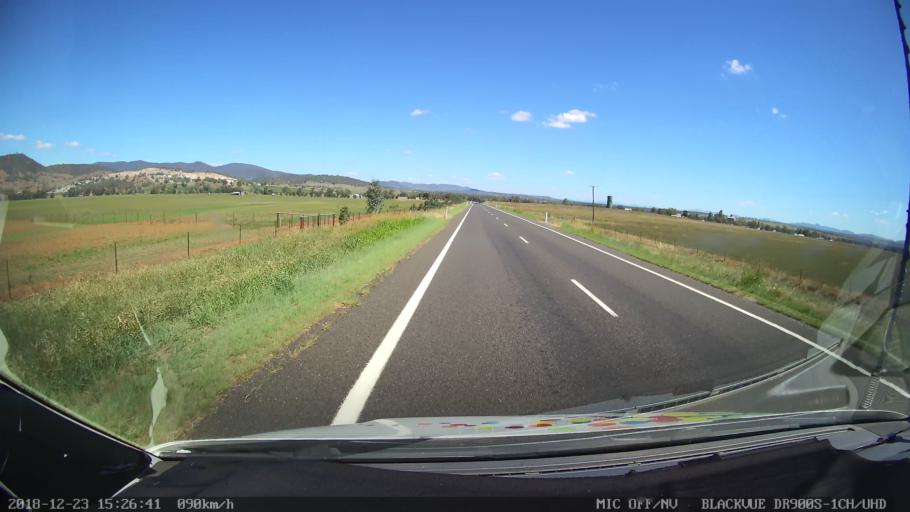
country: AU
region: New South Wales
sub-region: Tamworth Municipality
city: East Tamworth
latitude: -30.9198
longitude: 150.8403
